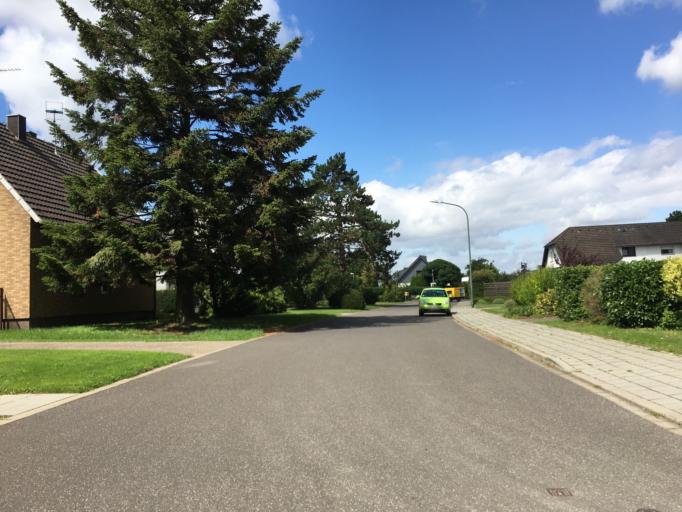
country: DE
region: North Rhine-Westphalia
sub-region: Regierungsbezirk Koln
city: Dueren
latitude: 50.7780
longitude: 6.4687
